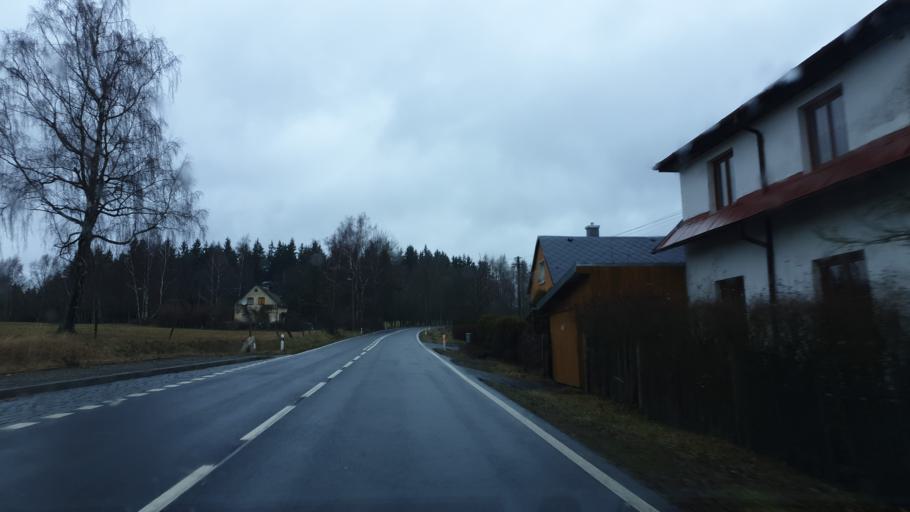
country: CZ
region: Karlovarsky
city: As
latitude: 50.2571
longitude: 12.1787
